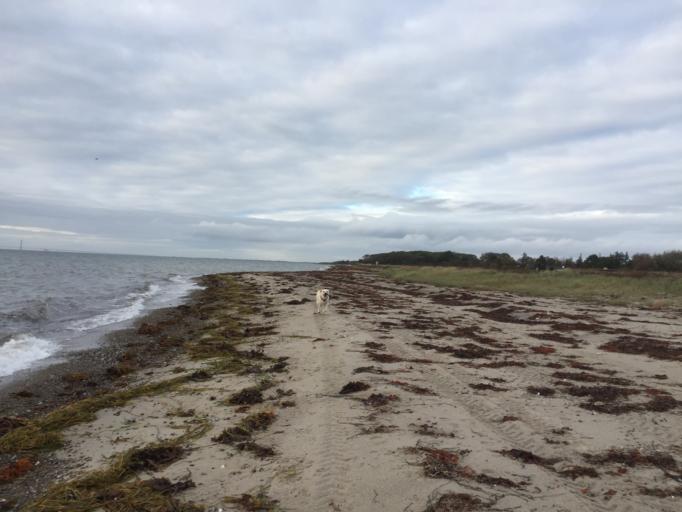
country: DK
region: Zealand
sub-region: Slagelse Kommune
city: Korsor
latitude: 55.2158
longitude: 11.1722
